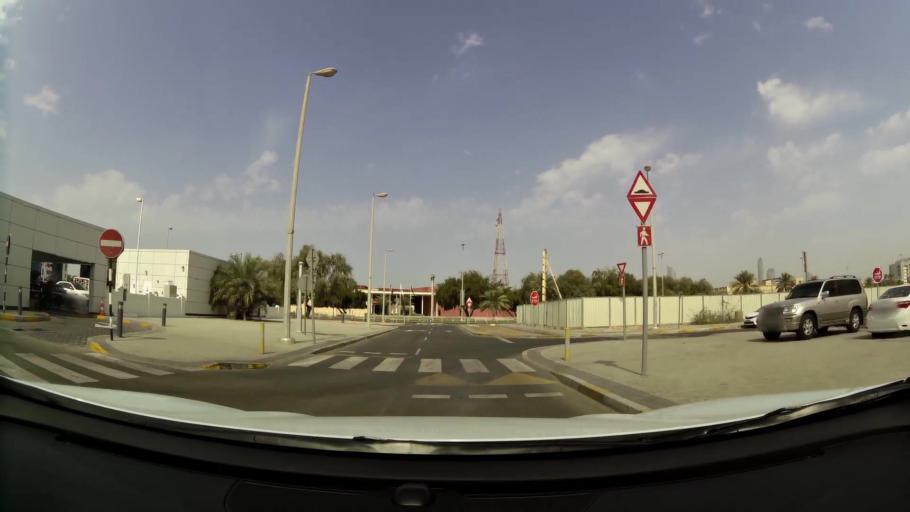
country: AE
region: Abu Dhabi
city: Abu Dhabi
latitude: 24.4570
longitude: 54.3571
